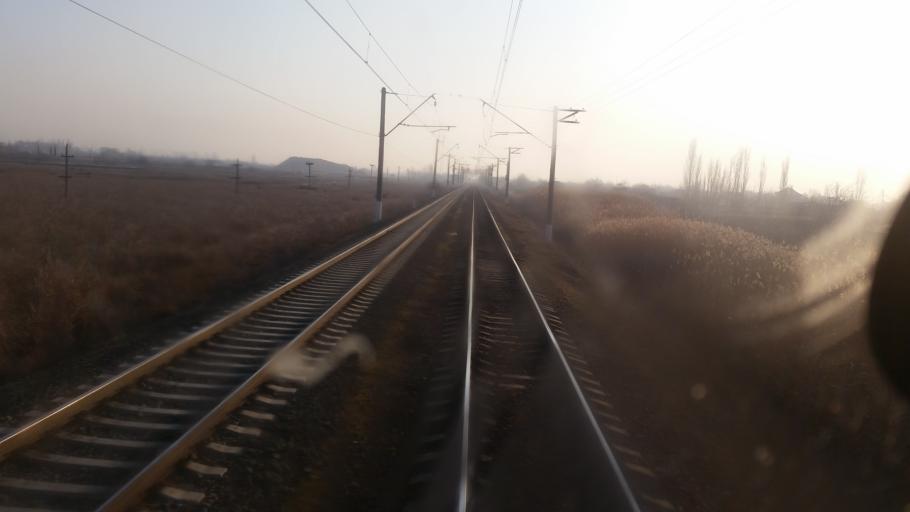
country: AZ
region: Yevlax
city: Aran
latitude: 40.6385
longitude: 46.9883
